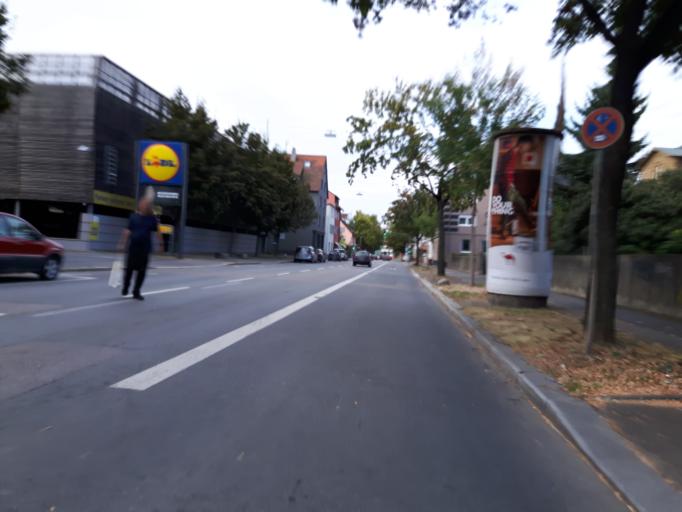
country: DE
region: Baden-Wuerttemberg
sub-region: Regierungsbezirk Stuttgart
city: Heilbronn
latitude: 49.1349
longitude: 9.2208
